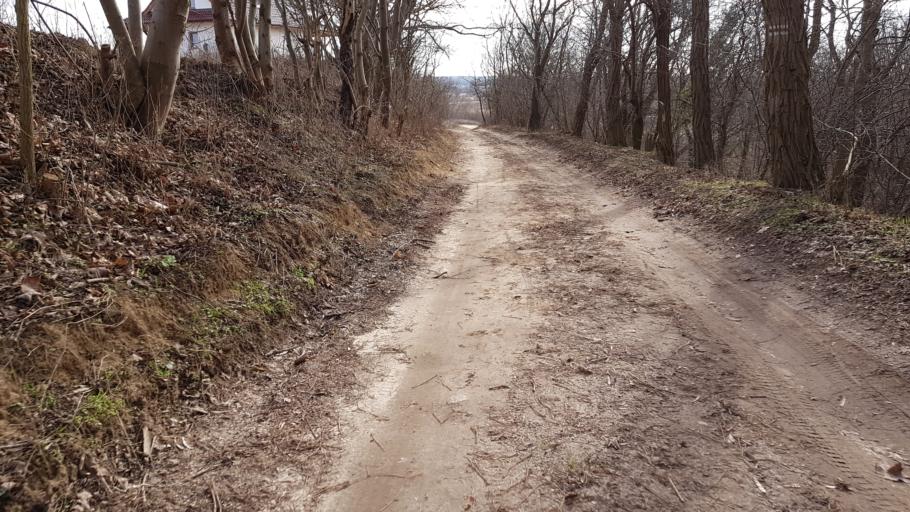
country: PL
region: West Pomeranian Voivodeship
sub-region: Powiat gryfinski
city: Gryfino
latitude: 53.2424
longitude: 14.4927
